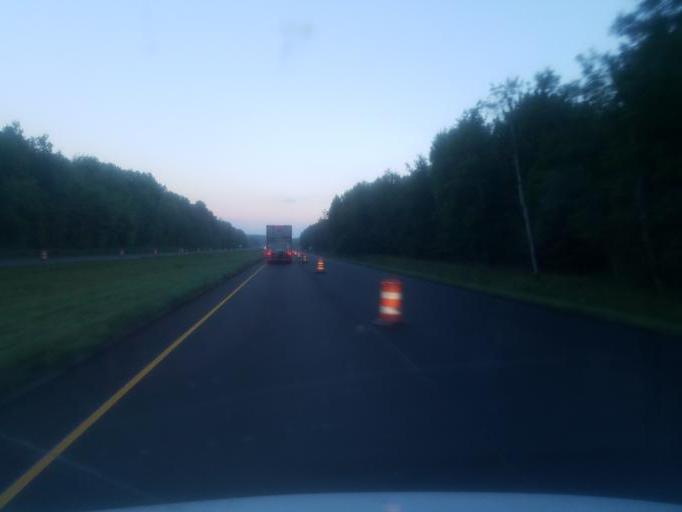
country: US
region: Ohio
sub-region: Ashtabula County
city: Jefferson
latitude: 41.7754
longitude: -80.7281
